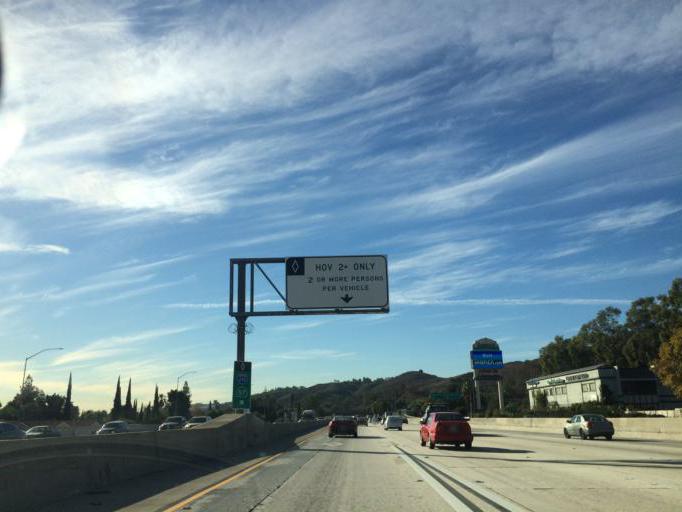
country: US
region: California
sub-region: Los Angeles County
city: La Verne
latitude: 34.0730
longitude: -117.7802
